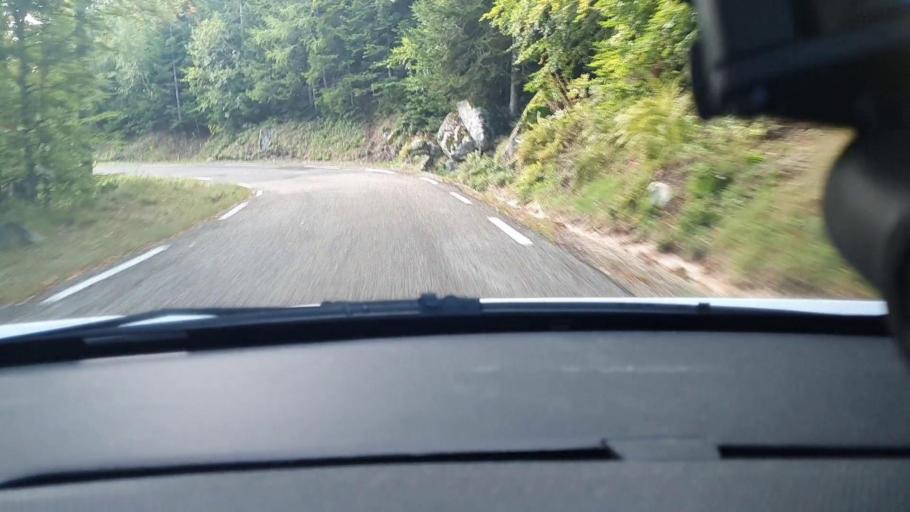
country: FR
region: Languedoc-Roussillon
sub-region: Departement du Gard
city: Branoux-les-Taillades
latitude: 44.3732
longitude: 3.9124
